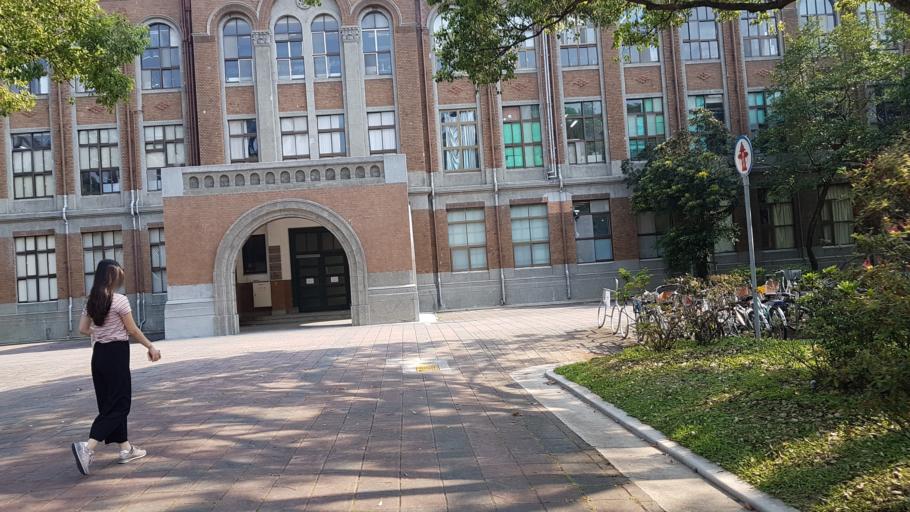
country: TW
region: Taipei
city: Taipei
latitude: 25.0172
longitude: 121.5359
